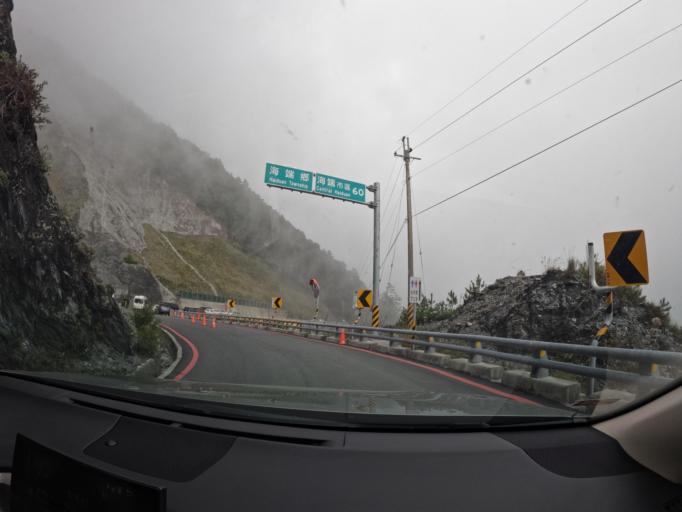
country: TW
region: Taiwan
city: Yujing
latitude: 23.2650
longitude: 120.9627
